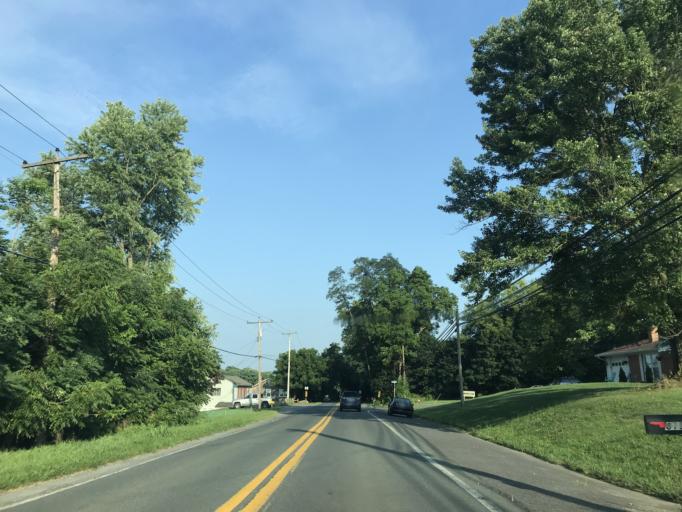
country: US
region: Maryland
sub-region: Carroll County
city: Westminster
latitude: 39.5559
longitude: -76.9664
